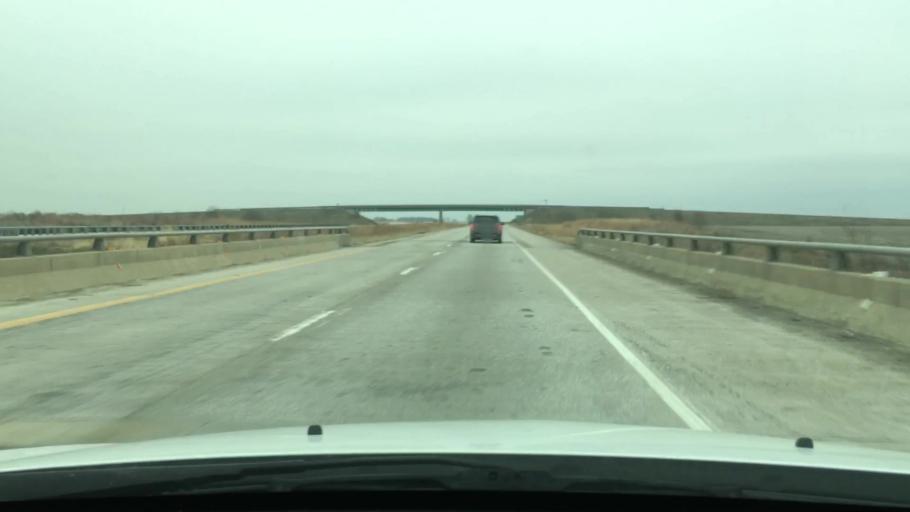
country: US
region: Illinois
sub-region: Sangamon County
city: New Berlin
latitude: 39.7368
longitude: -89.9889
